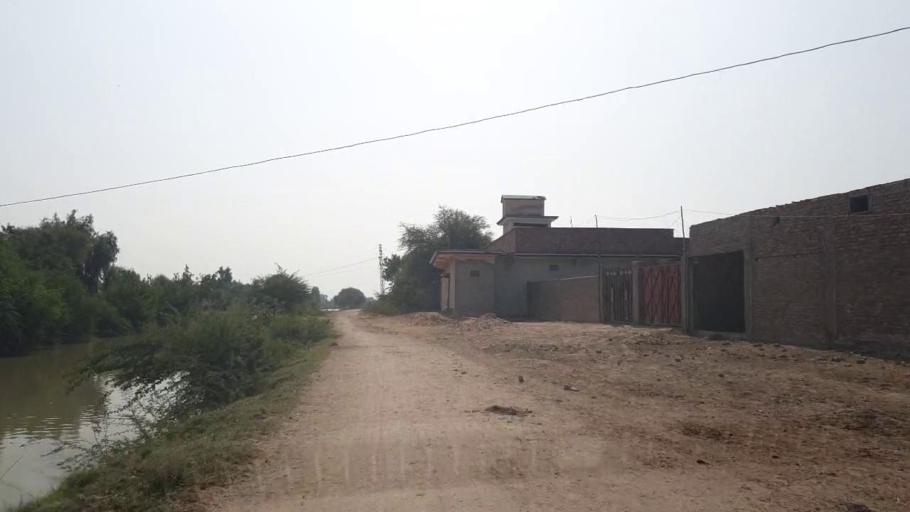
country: PK
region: Sindh
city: Badin
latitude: 24.6483
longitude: 68.8459
